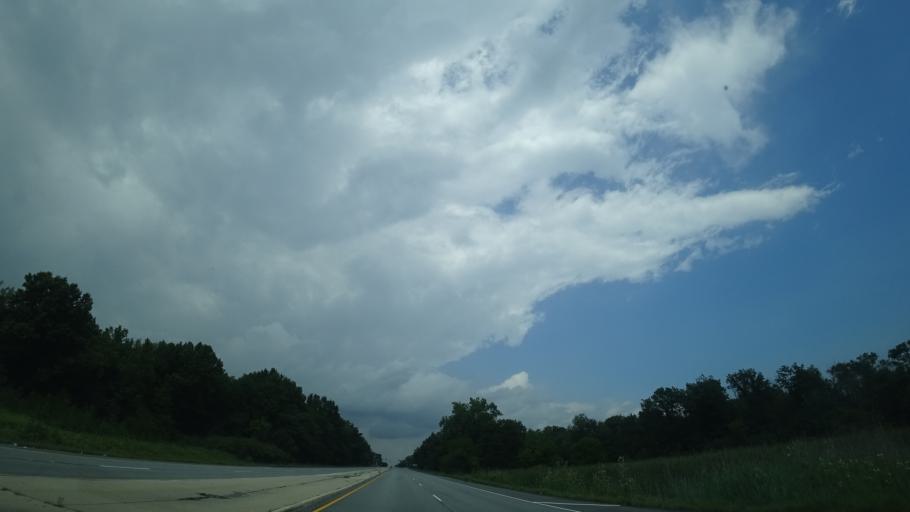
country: US
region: Illinois
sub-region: Cook County
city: Country Club Hills
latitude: 41.5390
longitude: -87.7326
